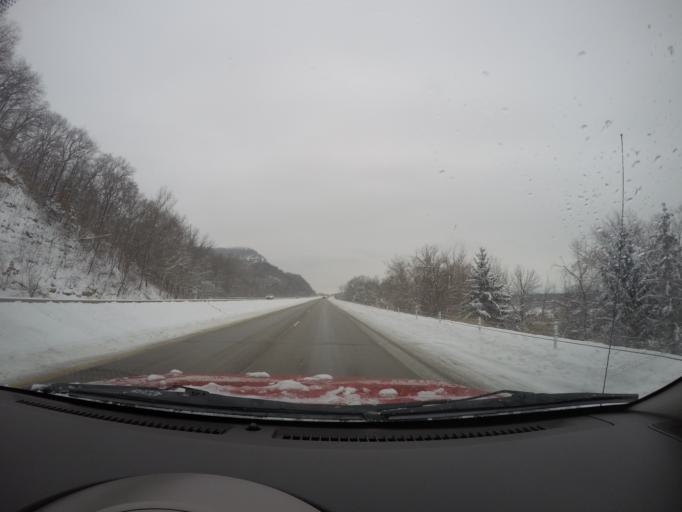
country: US
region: Wisconsin
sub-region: La Crosse County
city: Brice Prairie
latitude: 43.8953
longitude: -91.3444
